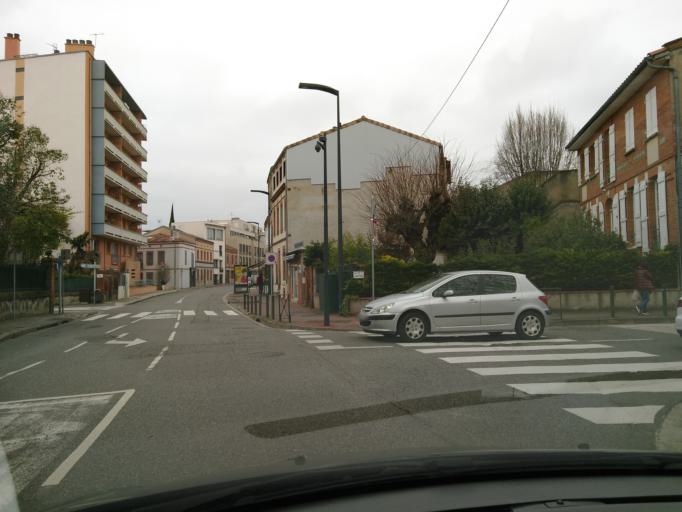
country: FR
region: Midi-Pyrenees
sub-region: Departement de la Haute-Garonne
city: Toulouse
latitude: 43.5941
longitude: 1.4656
